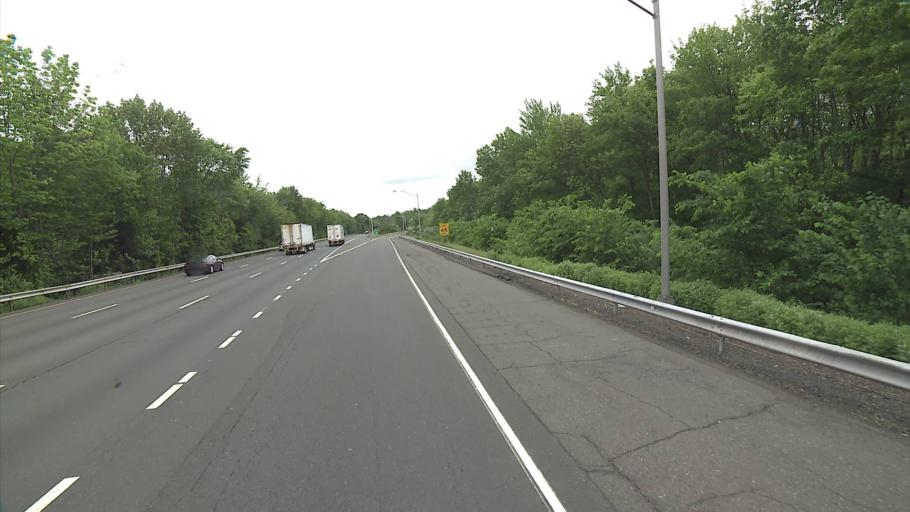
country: US
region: Connecticut
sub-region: Middlesex County
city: Cromwell
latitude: 41.6168
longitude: -72.6959
